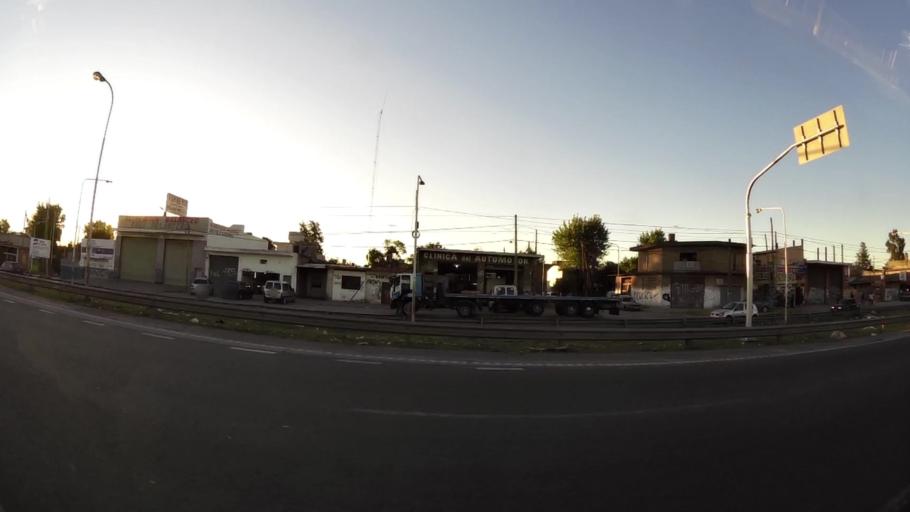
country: AR
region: Buenos Aires
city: Pontevedra
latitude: -34.7667
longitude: -58.6184
